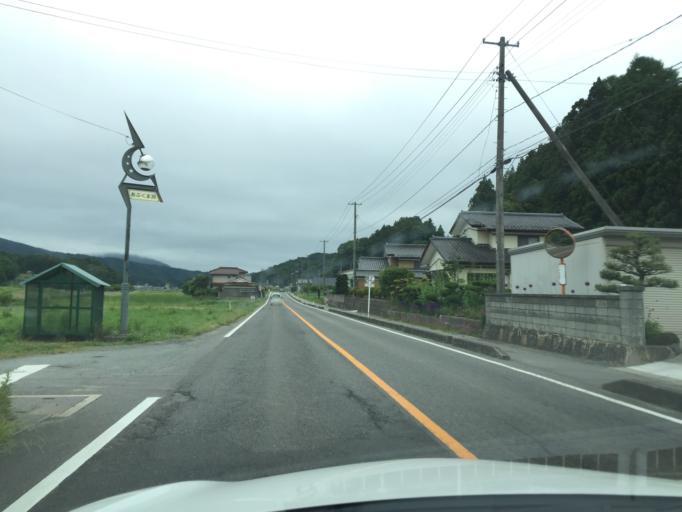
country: JP
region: Fukushima
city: Funehikimachi-funehiki
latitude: 37.3438
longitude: 140.6520
